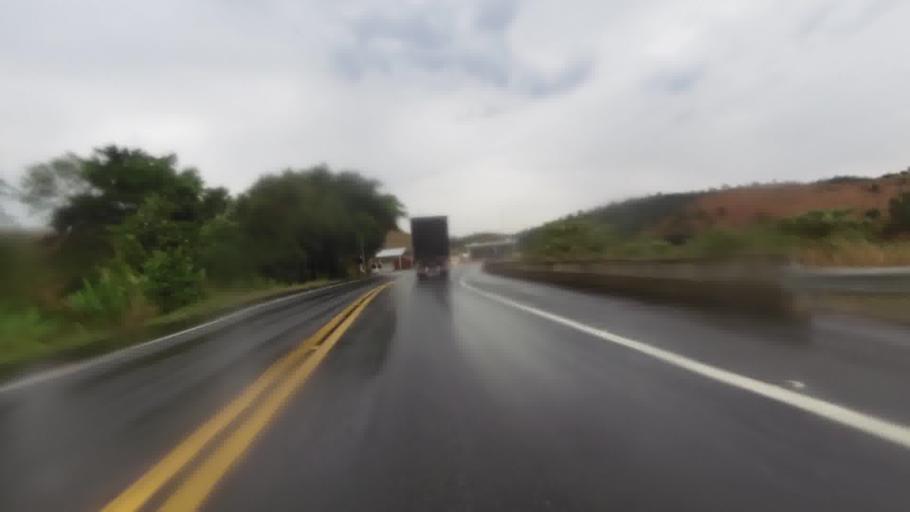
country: BR
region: Espirito Santo
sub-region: Mimoso Do Sul
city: Mimoso do Sul
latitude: -21.1569
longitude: -41.2781
